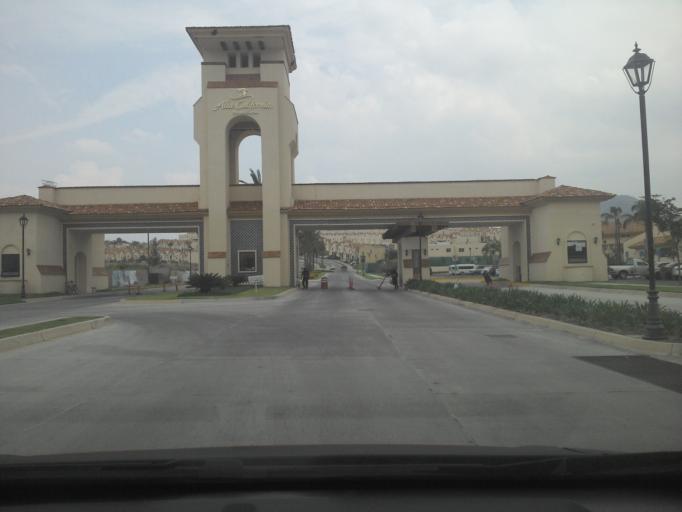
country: MX
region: Jalisco
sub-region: Tlajomulco de Zuniga
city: Lomas de San Agustin
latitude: 20.5292
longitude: -103.4635
